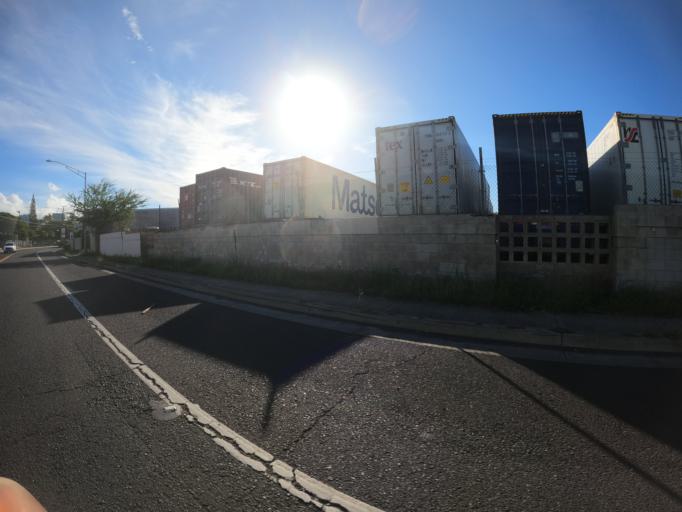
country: US
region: Hawaii
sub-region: Honolulu County
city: Honolulu
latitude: 21.3064
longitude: -157.8765
